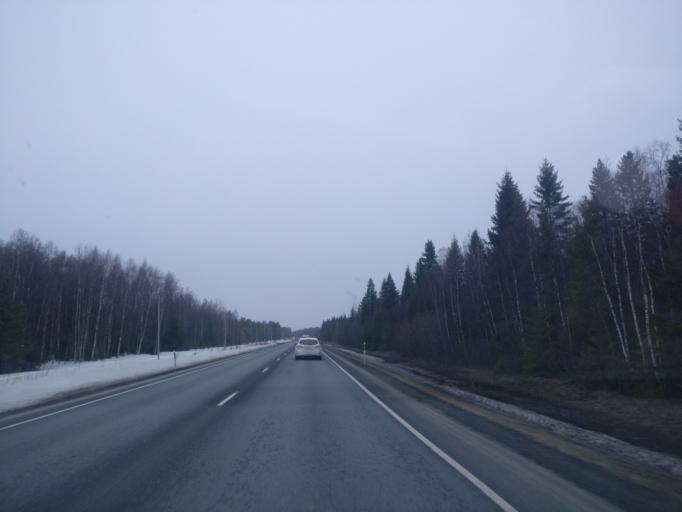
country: FI
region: Lapland
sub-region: Kemi-Tornio
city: Simo
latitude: 65.6712
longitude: 24.9176
